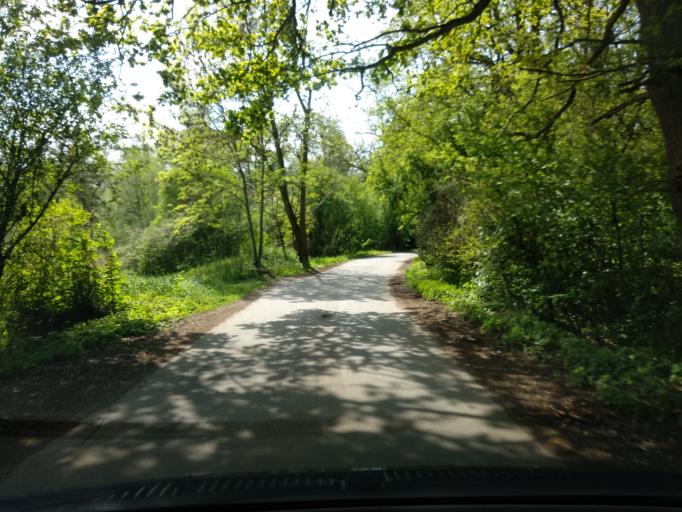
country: PL
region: Lower Silesian Voivodeship
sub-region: Powiat trzebnicki
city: Psary
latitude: 51.1576
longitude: 17.0782
